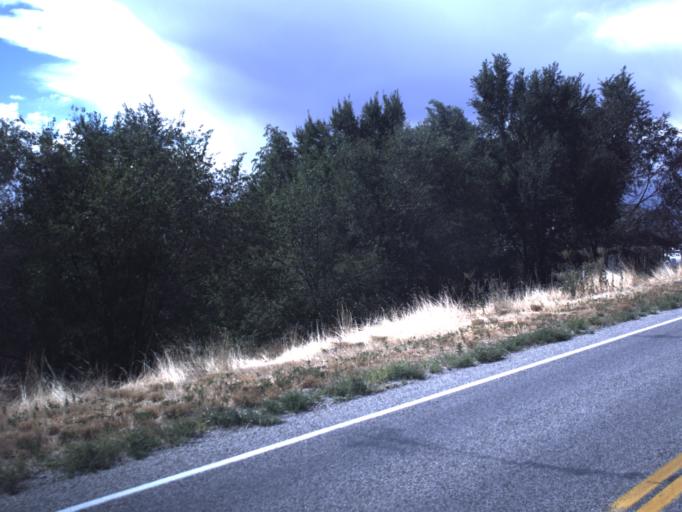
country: US
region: Utah
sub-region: Box Elder County
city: Elwood
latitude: 41.7232
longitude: -112.0952
